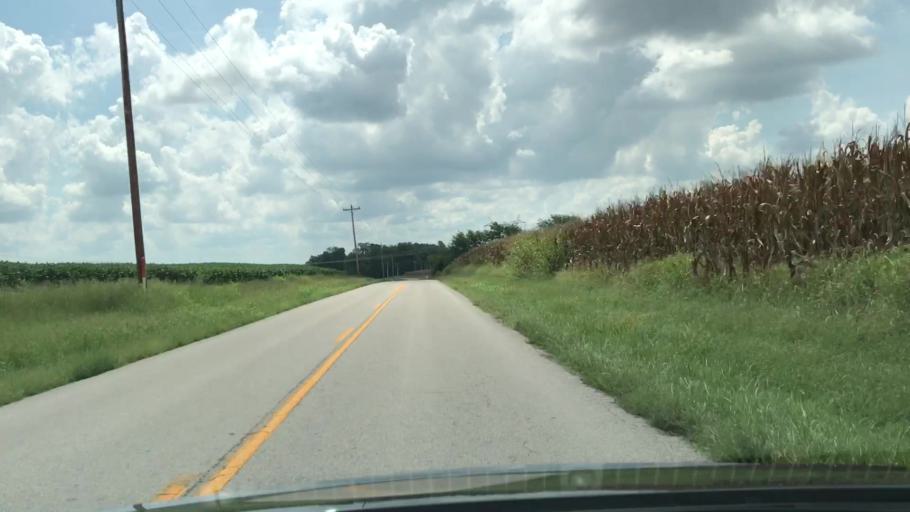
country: US
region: Kentucky
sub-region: Todd County
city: Elkton
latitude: 36.7761
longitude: -87.1191
